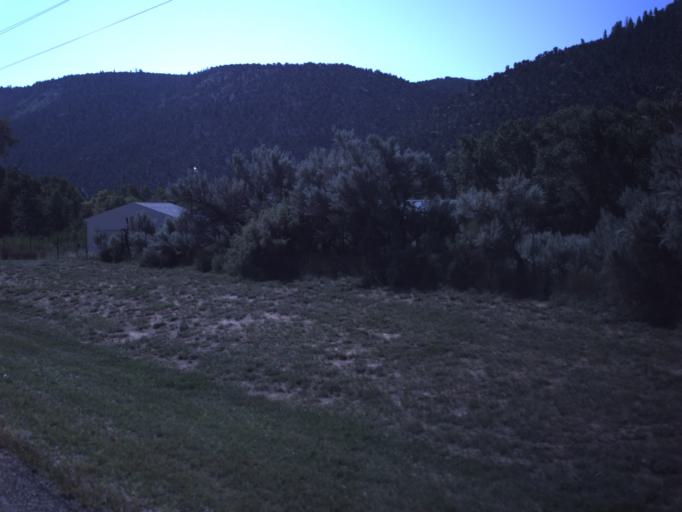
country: US
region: Utah
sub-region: Duchesne County
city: Duchesne
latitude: 40.3062
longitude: -110.6299
